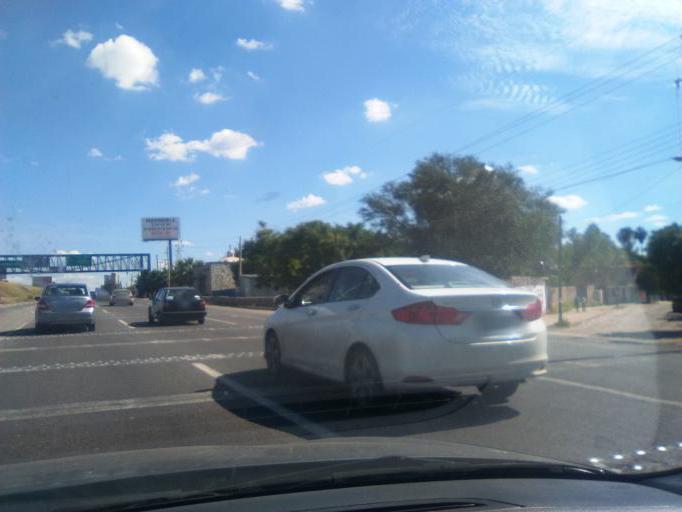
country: MX
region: Guanajuato
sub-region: Silao de la Victoria
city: El Refugio de los Sauces
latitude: 21.0252
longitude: -101.5399
